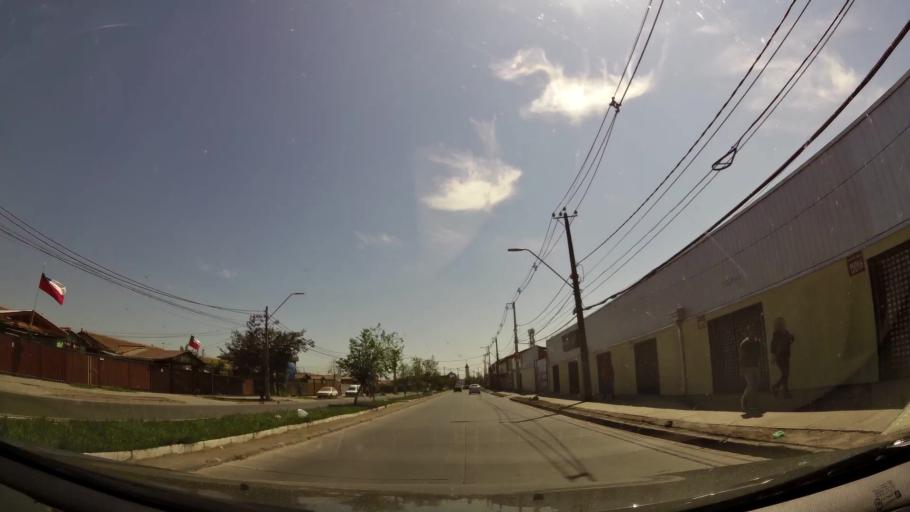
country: CL
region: Santiago Metropolitan
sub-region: Provincia de Santiago
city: Lo Prado
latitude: -33.4017
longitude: -70.7458
